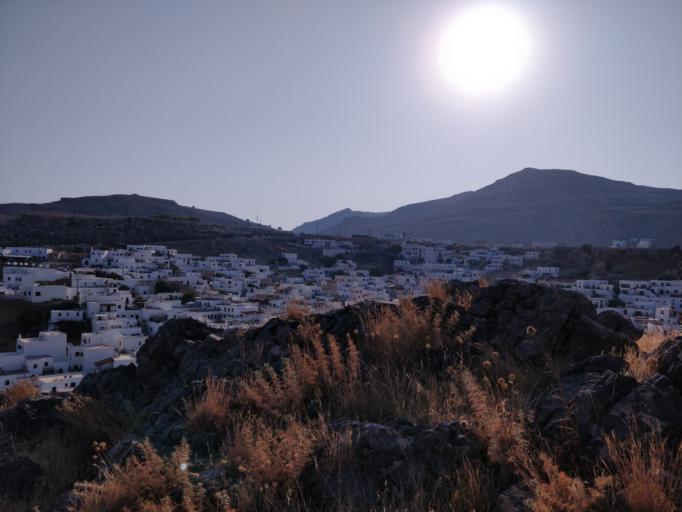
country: GR
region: South Aegean
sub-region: Nomos Dodekanisou
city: Lardos
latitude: 36.0900
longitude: 28.0879
